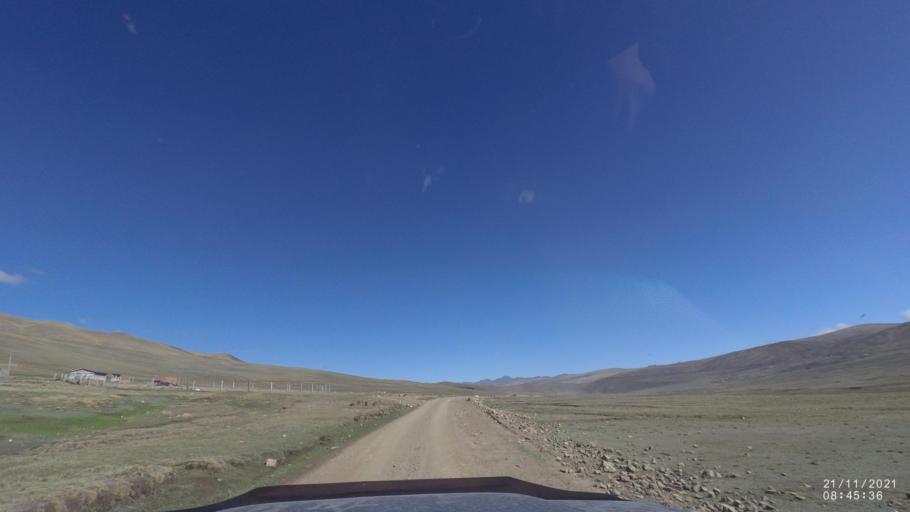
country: BO
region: Cochabamba
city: Cochabamba
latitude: -17.2477
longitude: -66.2320
